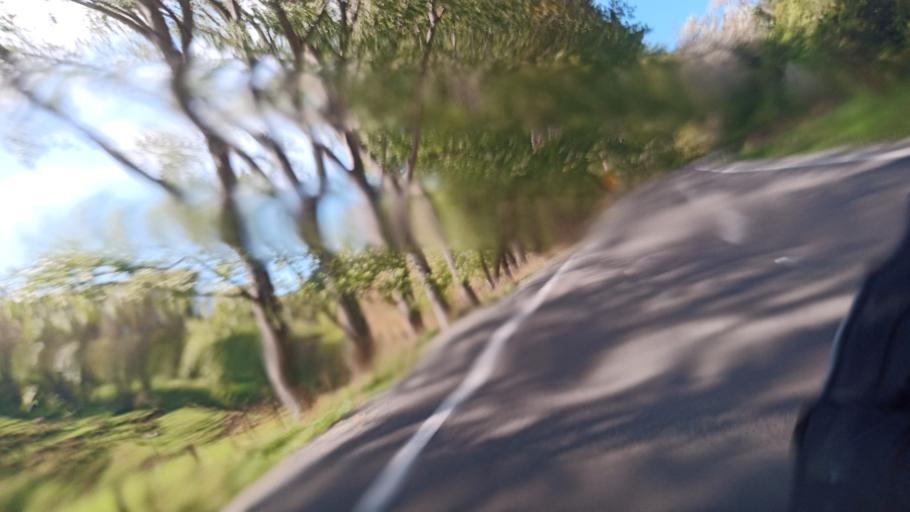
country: NZ
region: Gisborne
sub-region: Gisborne District
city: Gisborne
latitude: -38.4695
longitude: 178.2551
